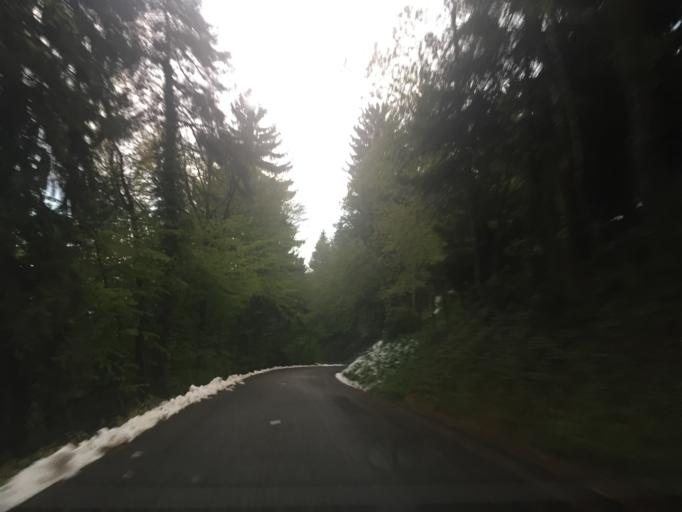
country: FR
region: Rhone-Alpes
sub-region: Departement de la Savoie
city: La Motte-Servolex
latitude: 45.5853
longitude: 5.8304
